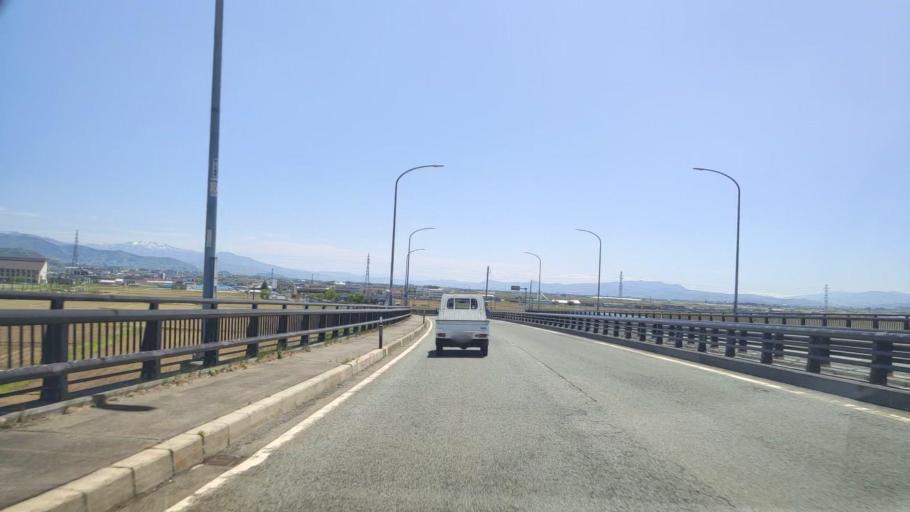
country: JP
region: Yamagata
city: Higashine
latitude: 38.4933
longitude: 140.3838
